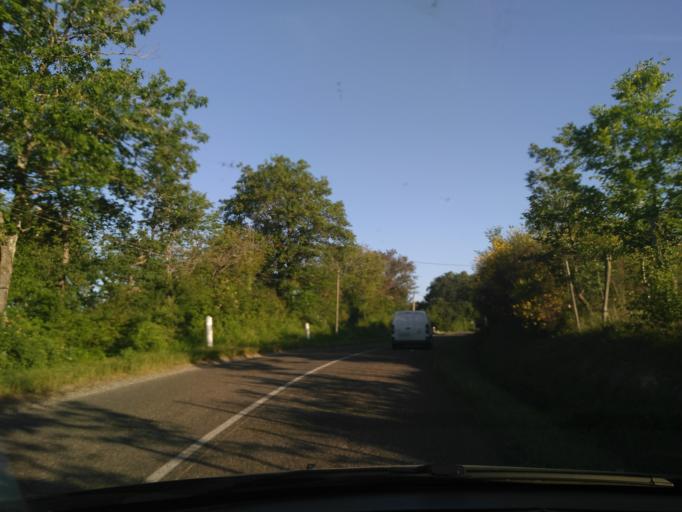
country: FR
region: Midi-Pyrenees
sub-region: Departement du Gers
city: Valence-sur-Baise
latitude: 43.8709
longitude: 0.4689
